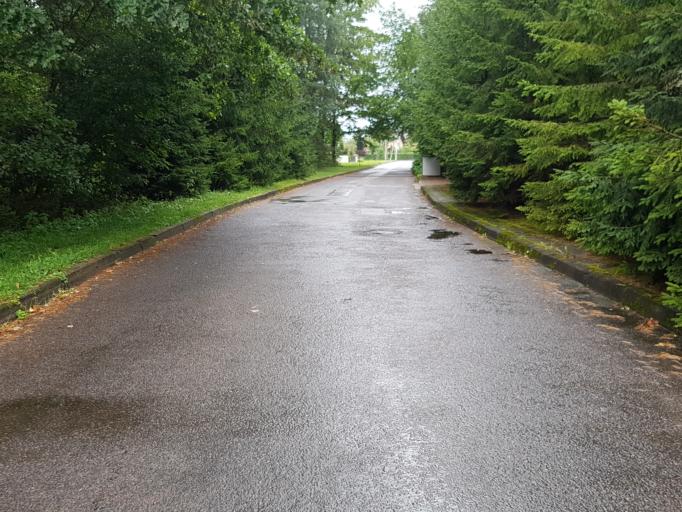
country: LT
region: Vilnius County
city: Lazdynai
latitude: 54.6612
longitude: 25.1852
